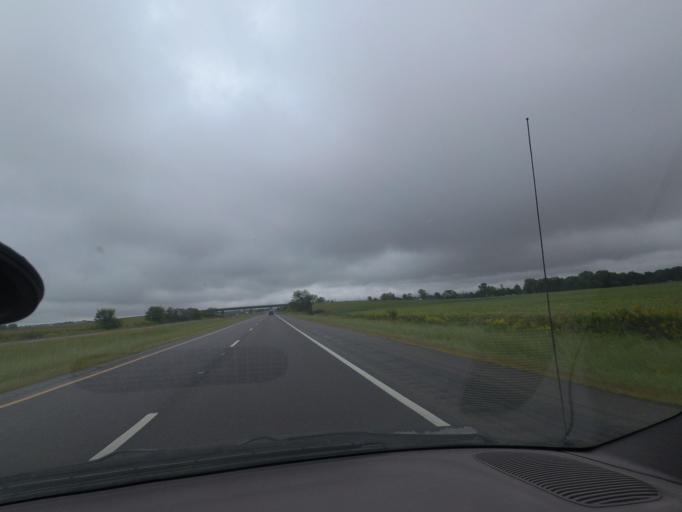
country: US
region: Illinois
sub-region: Champaign County
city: Lake of the Woods
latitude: 40.1204
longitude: -88.3361
